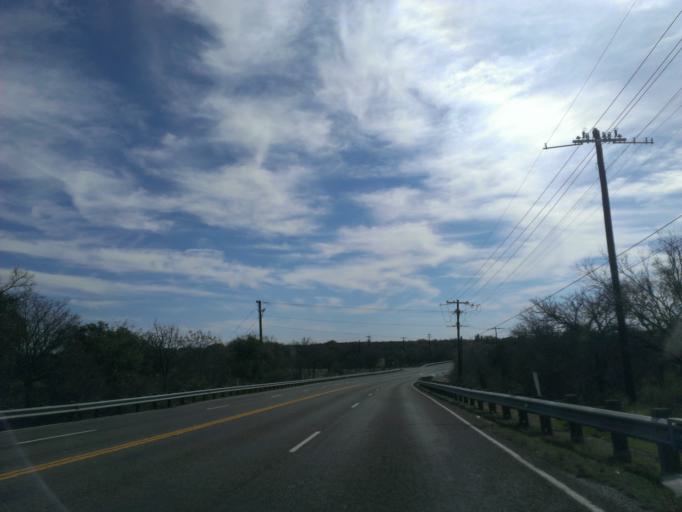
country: US
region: Texas
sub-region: Llano County
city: Kingsland
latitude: 30.6407
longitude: -98.4105
